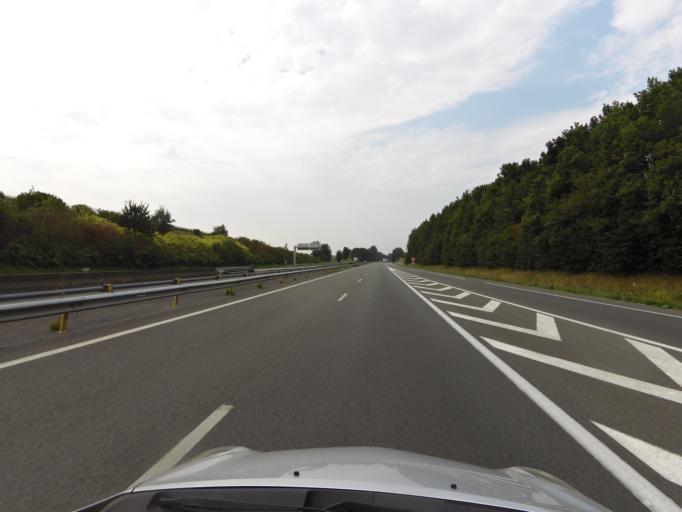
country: FR
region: Nord-Pas-de-Calais
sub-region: Departement du Pas-de-Calais
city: Bourlon
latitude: 50.1456
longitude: 3.1250
